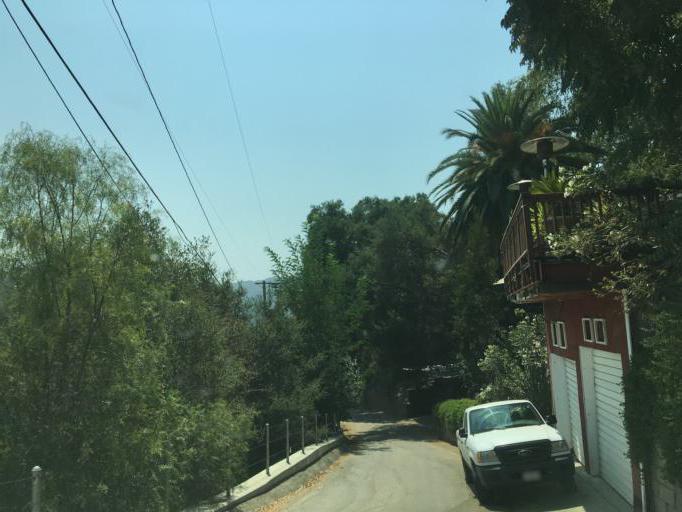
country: US
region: California
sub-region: Los Angeles County
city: Topanga
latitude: 34.0979
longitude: -118.6013
